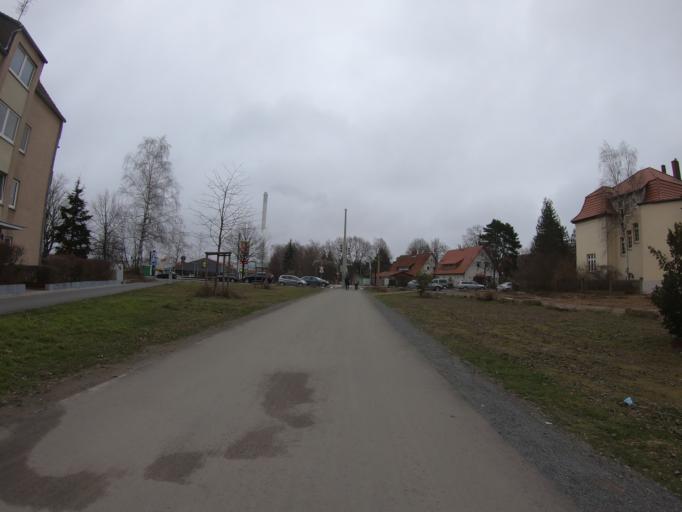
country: DE
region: Lower Saxony
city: Braunschweig
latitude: 52.2764
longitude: 10.5043
